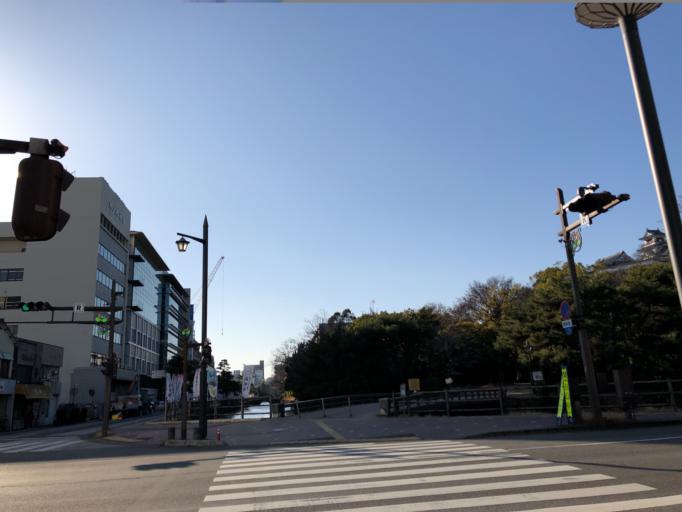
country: JP
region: Kochi
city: Kochi-shi
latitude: 33.5597
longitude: 133.5341
